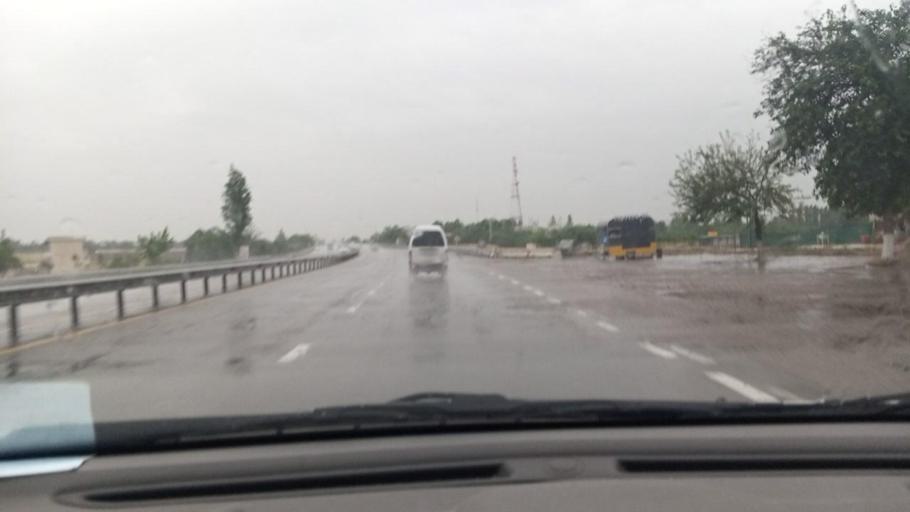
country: UZ
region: Toshkent
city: Tuytepa
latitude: 41.1269
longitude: 69.4374
